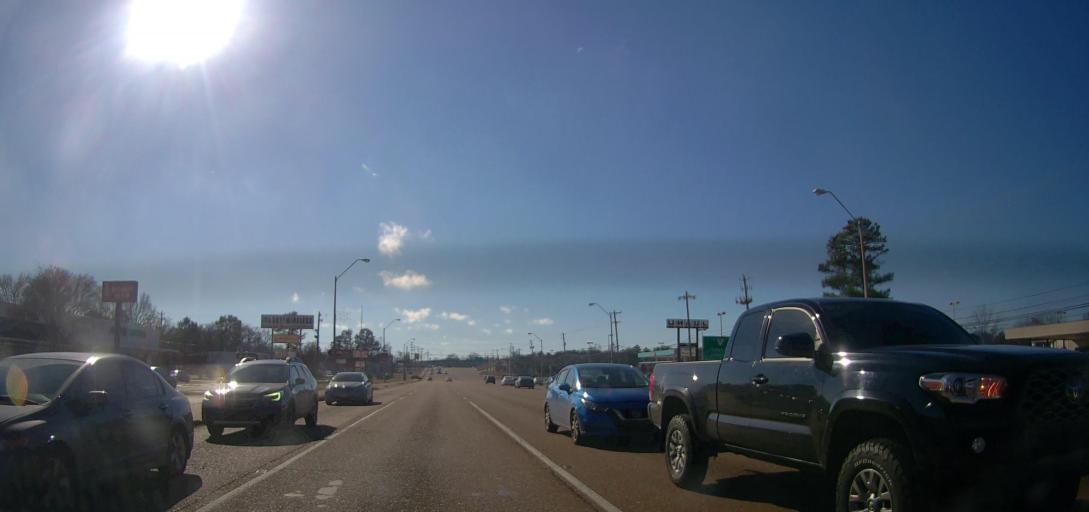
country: US
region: Tennessee
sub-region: Shelby County
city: Bartlett
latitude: 35.2135
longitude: -89.9167
